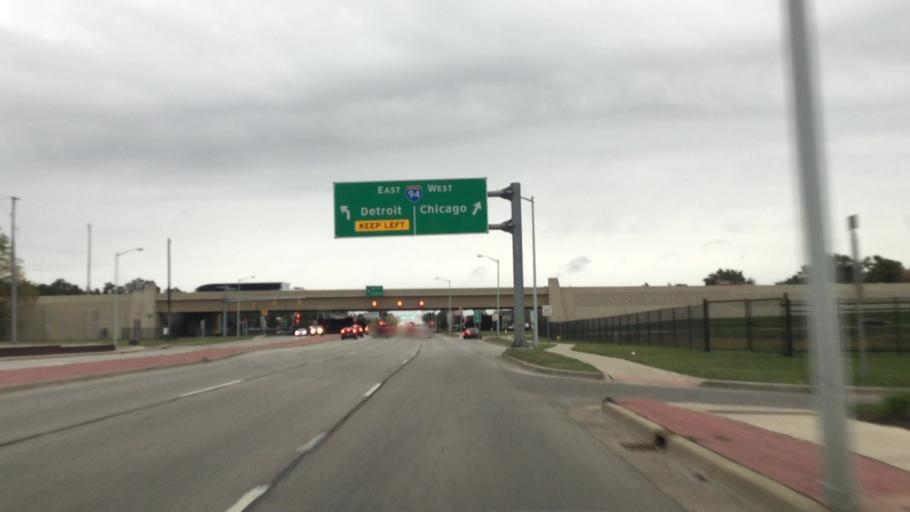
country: US
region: Michigan
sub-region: Kalamazoo County
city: Portage
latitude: 42.2387
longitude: -85.5897
